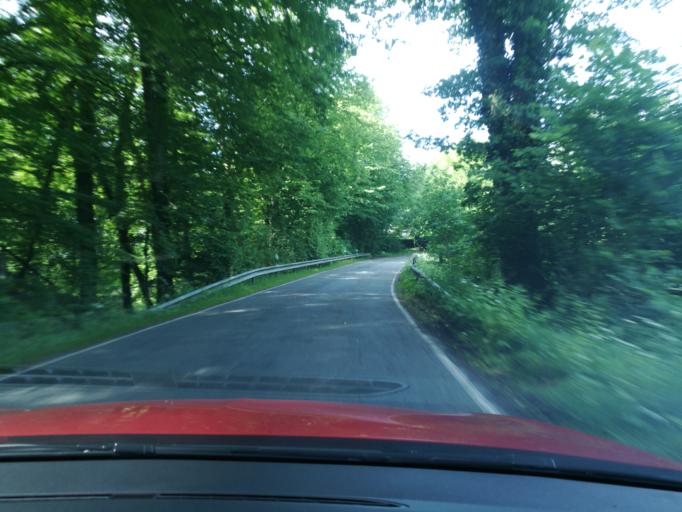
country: DE
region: Schleswig-Holstein
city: Lasbek
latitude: 53.7444
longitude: 10.3403
